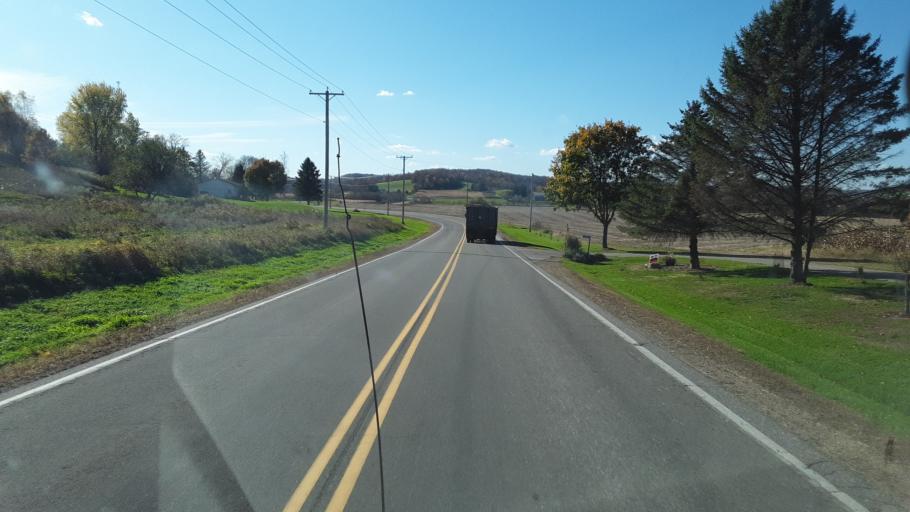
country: US
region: Wisconsin
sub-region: Sauk County
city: Reedsburg
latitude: 43.5413
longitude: -90.1556
